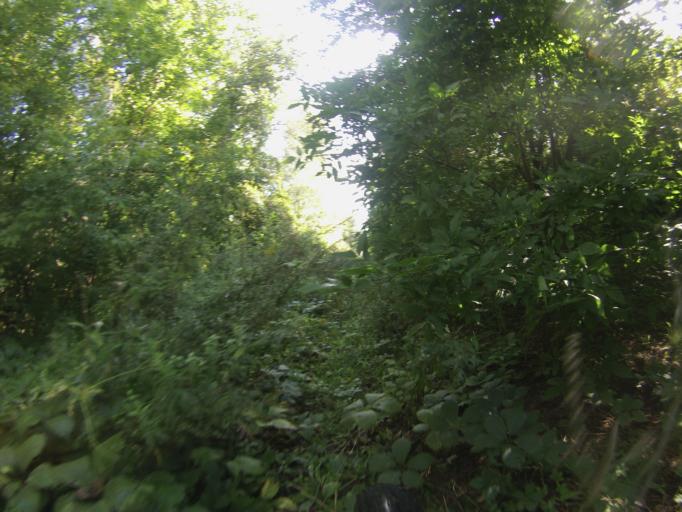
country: CA
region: Ontario
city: Ottawa
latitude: 45.3700
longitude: -75.6333
